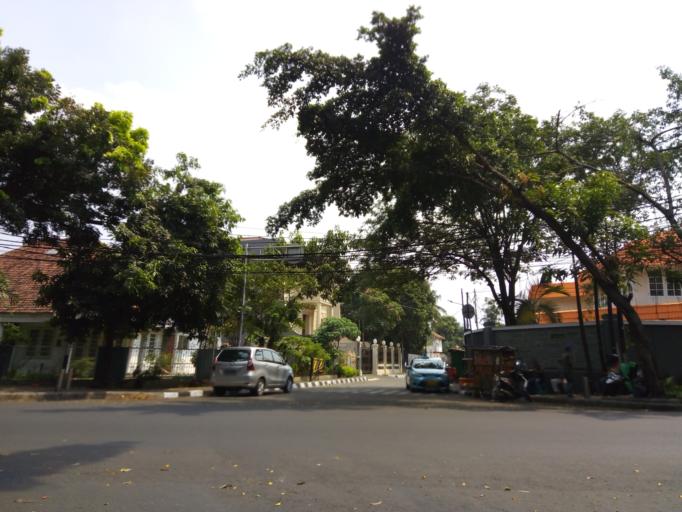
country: ID
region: Jakarta Raya
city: Jakarta
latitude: -6.2032
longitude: 106.8383
